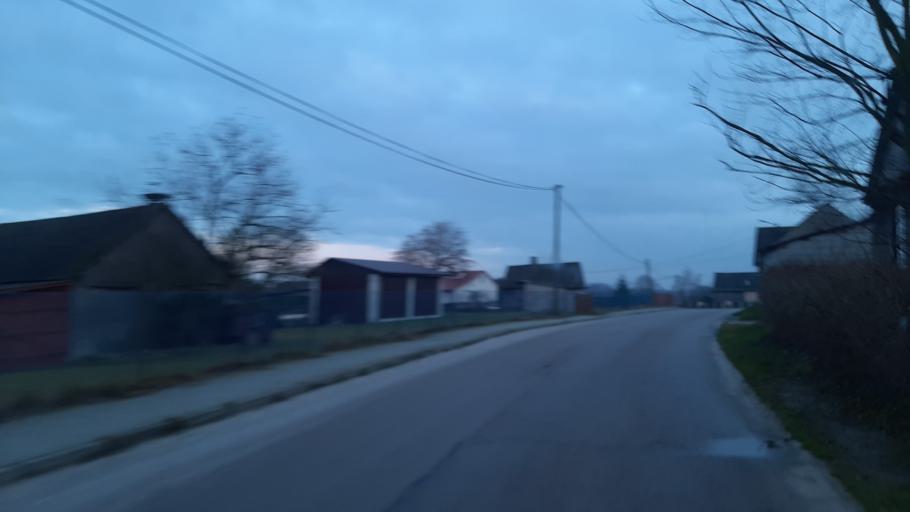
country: PL
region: Lublin Voivodeship
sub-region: Powiat lubartowski
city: Firlej
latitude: 51.5688
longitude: 22.5312
